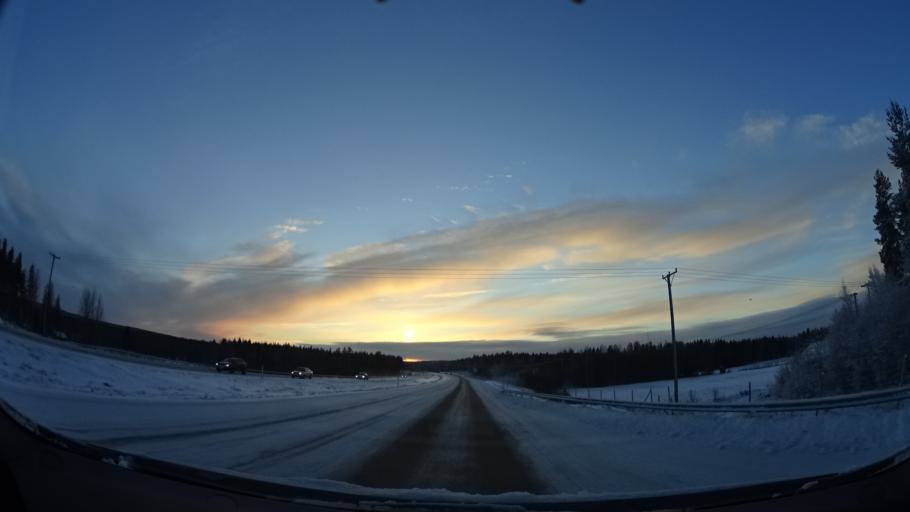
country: SE
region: Vaesterbotten
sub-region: Skelleftea Kommun
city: Kage
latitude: 64.8001
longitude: 21.0280
